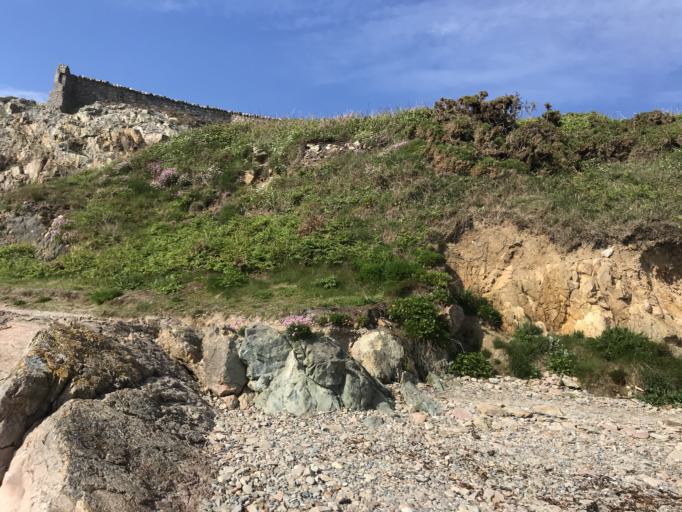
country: IE
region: Leinster
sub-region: Fingal County
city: Howth
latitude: 53.3654
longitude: -6.0881
